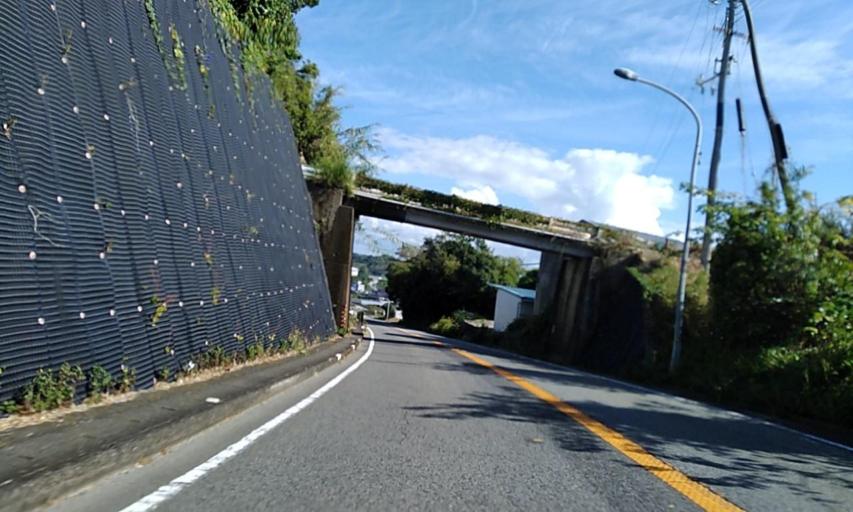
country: JP
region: Wakayama
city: Tanabe
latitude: 33.7822
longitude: 135.2735
